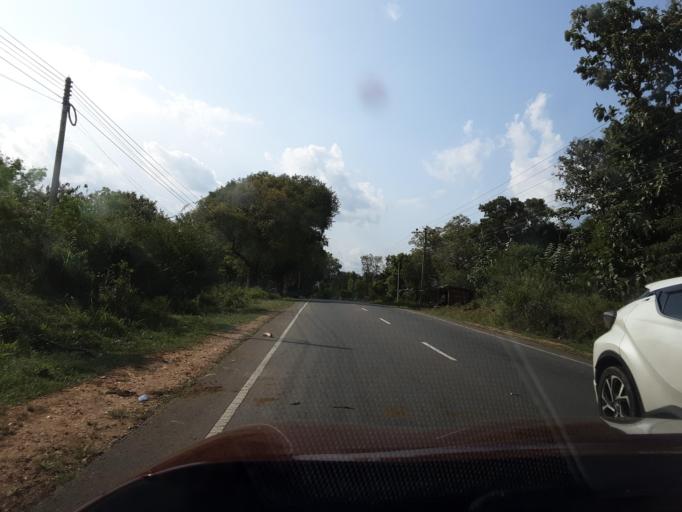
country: LK
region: Uva
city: Haputale
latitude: 6.6081
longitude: 81.1349
